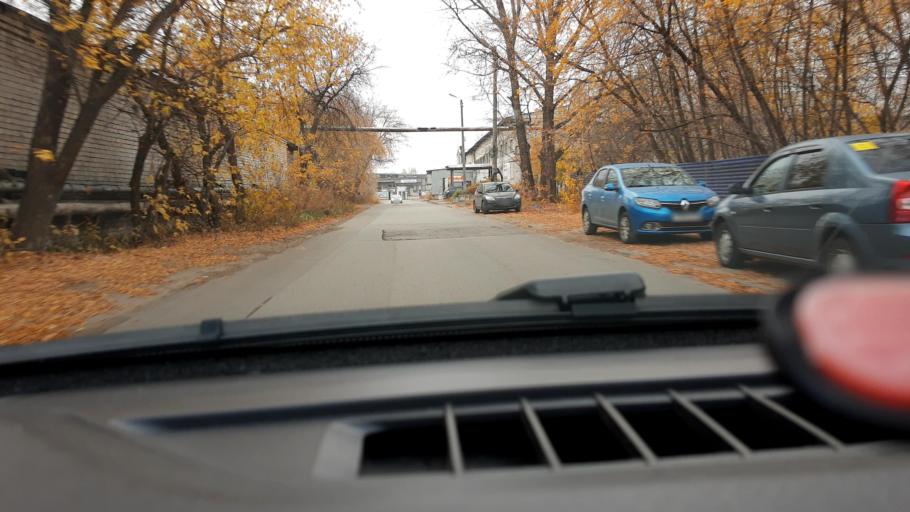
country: RU
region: Nizjnij Novgorod
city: Gorbatovka
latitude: 56.3408
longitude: 43.8191
